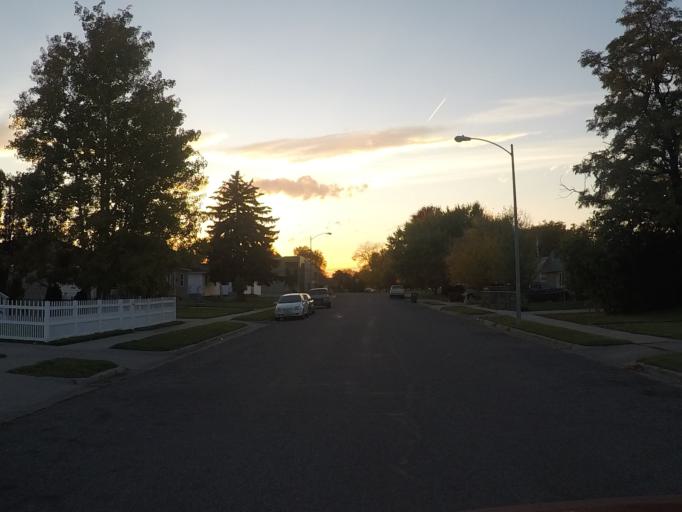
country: US
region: Montana
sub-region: Yellowstone County
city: Billings
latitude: 45.7869
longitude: -108.5470
